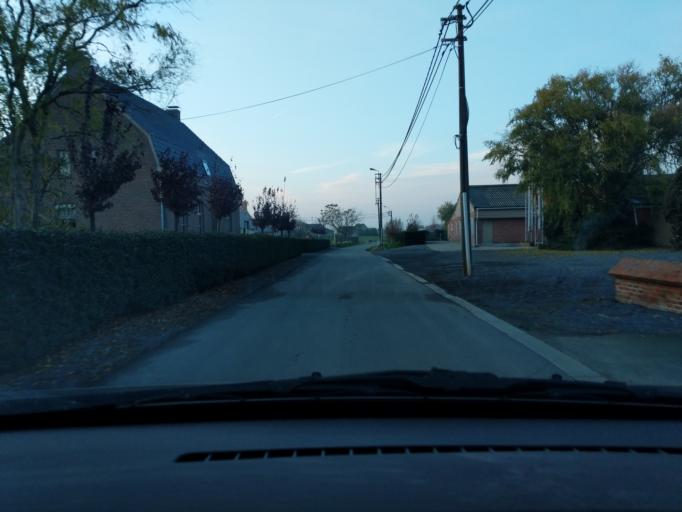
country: BE
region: Flanders
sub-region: Provincie Oost-Vlaanderen
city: Nevele
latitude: 51.0306
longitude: 3.5181
